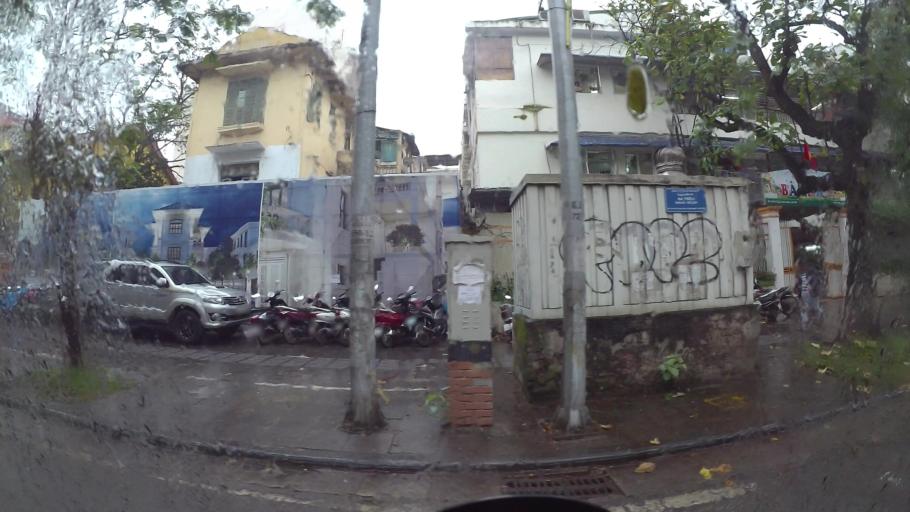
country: VN
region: Ha Noi
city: Hai BaTrung
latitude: 21.0193
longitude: 105.8496
